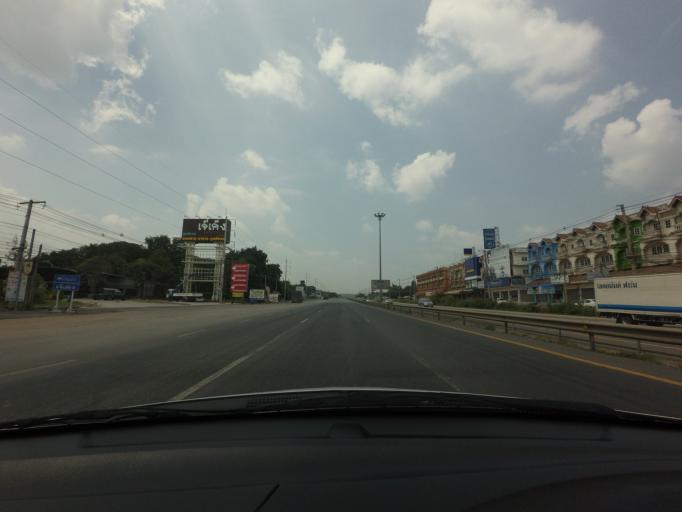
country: TH
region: Nakhon Ratchasima
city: Pak Chong
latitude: 14.6590
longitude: 101.3845
